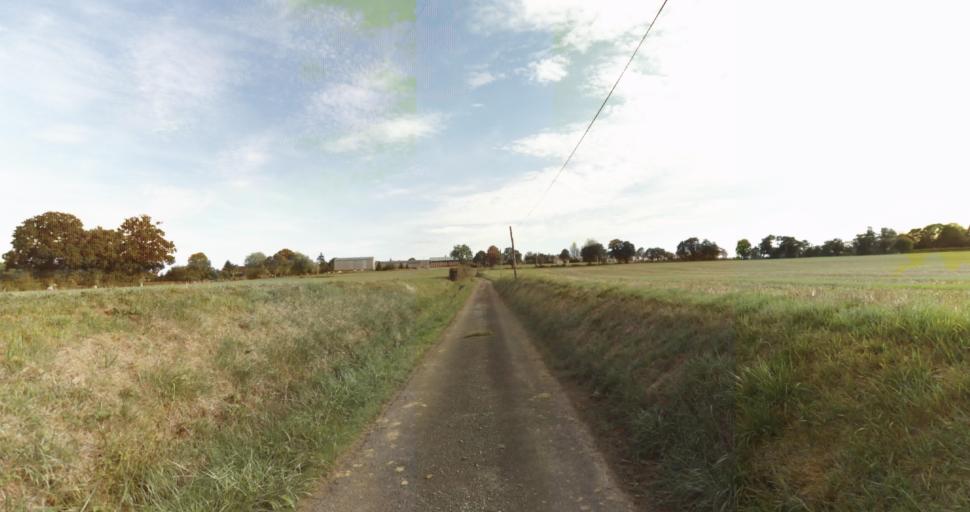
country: FR
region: Lower Normandy
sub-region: Departement de l'Orne
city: Gace
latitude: 48.7116
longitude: 0.2767
